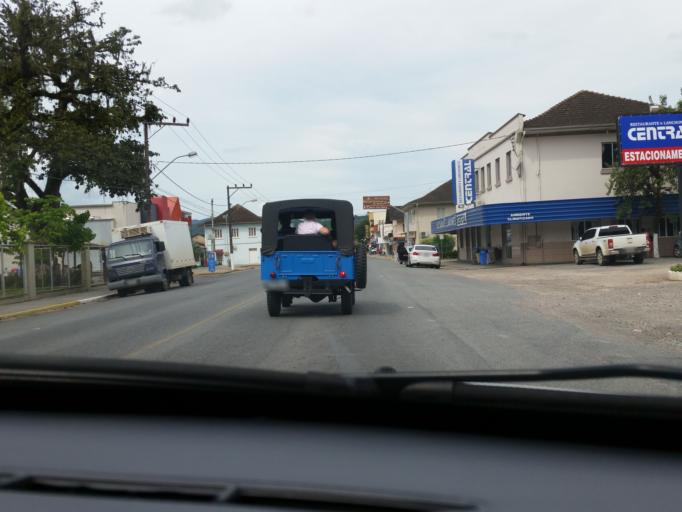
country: BR
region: Santa Catarina
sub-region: Rodeio
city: Gavea
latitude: -27.0344
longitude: -49.3881
